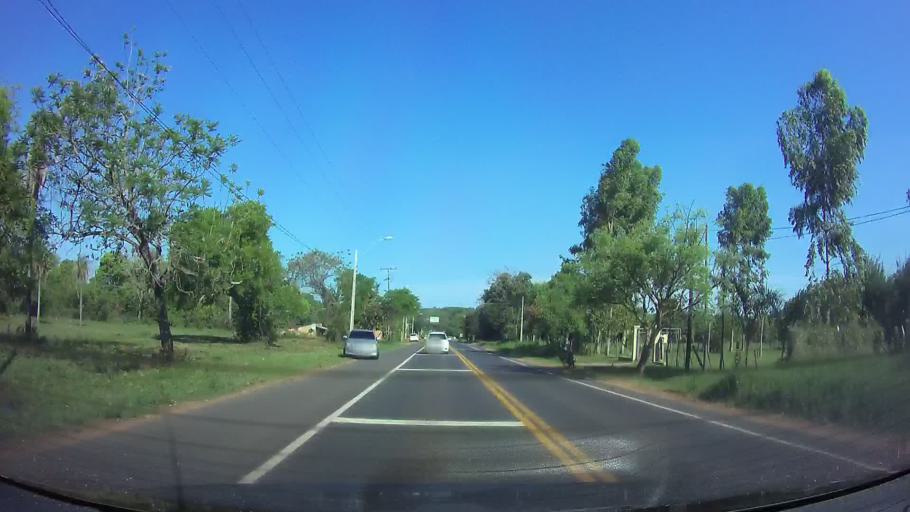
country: PY
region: Central
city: Itaugua
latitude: -25.3516
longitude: -57.3359
